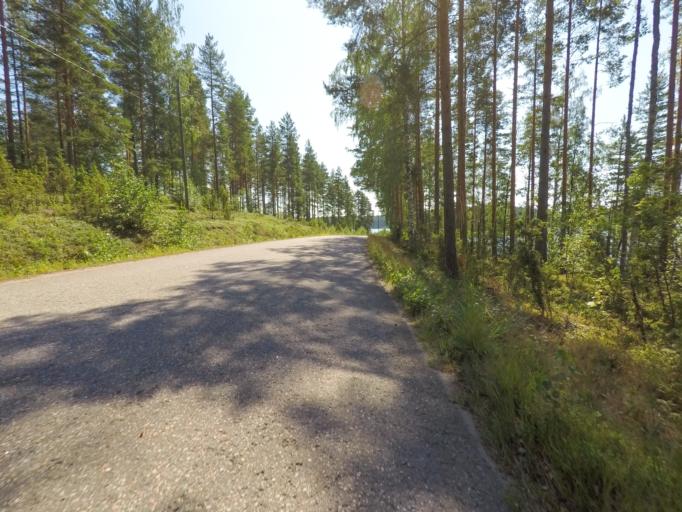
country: FI
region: Southern Savonia
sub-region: Mikkeli
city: Puumala
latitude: 61.4361
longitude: 28.1697
